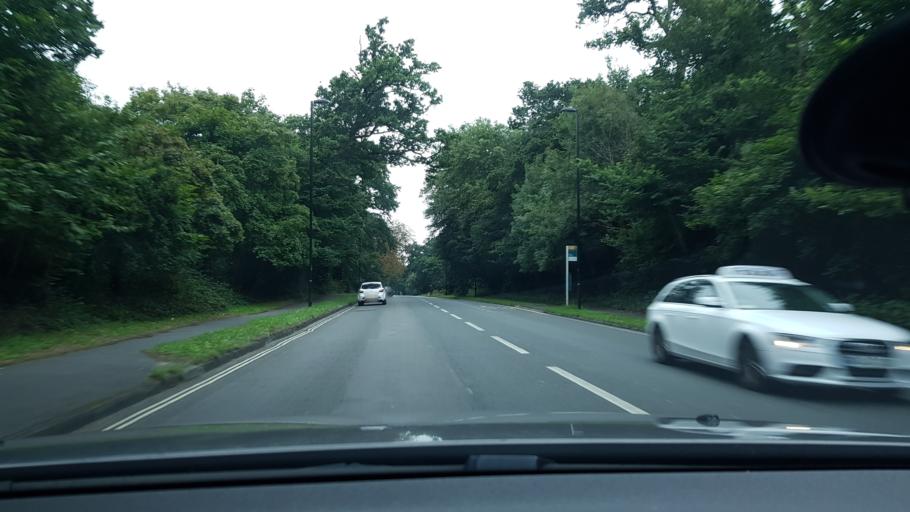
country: GB
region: England
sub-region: Southampton
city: Southampton
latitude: 50.9275
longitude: -1.4056
